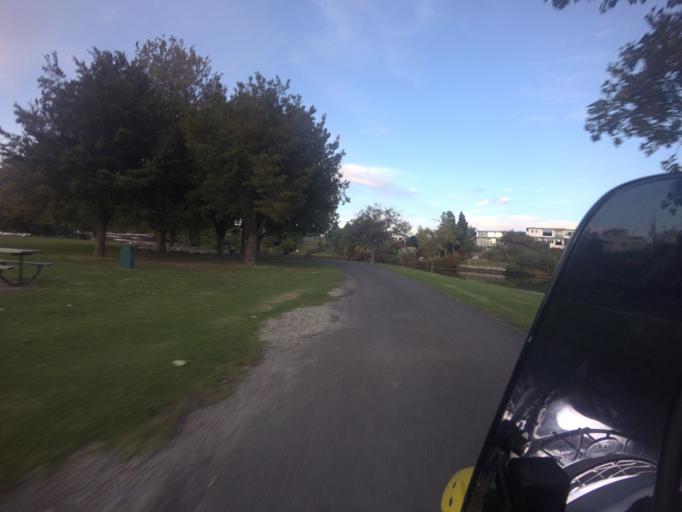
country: NZ
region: Gisborne
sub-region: Gisborne District
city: Gisborne
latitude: -38.6616
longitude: 178.0331
